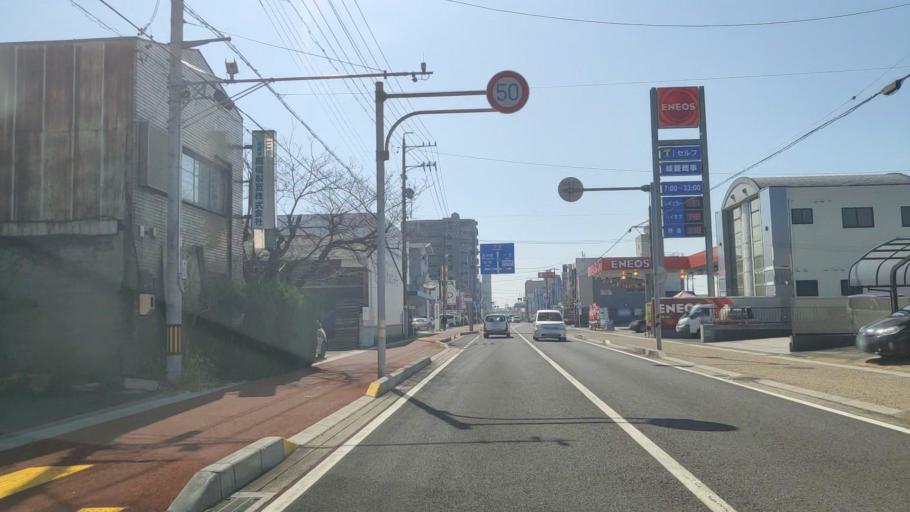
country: JP
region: Gifu
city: Gifu-shi
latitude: 35.3990
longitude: 136.7658
